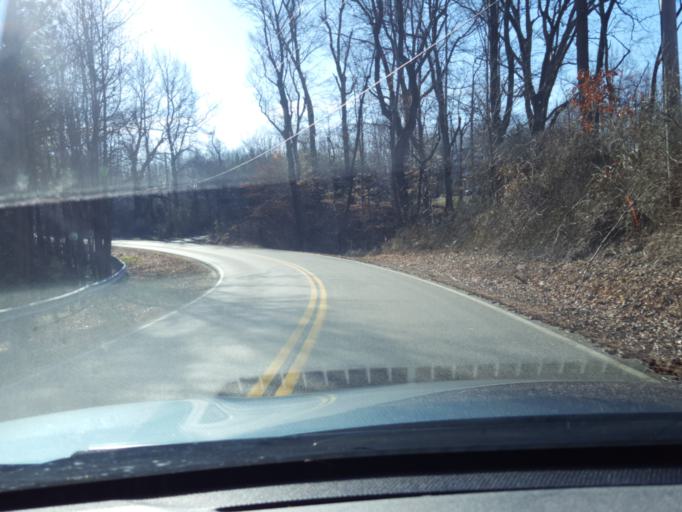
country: US
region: Maryland
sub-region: Calvert County
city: Chesapeake Beach
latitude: 38.6396
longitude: -76.5408
